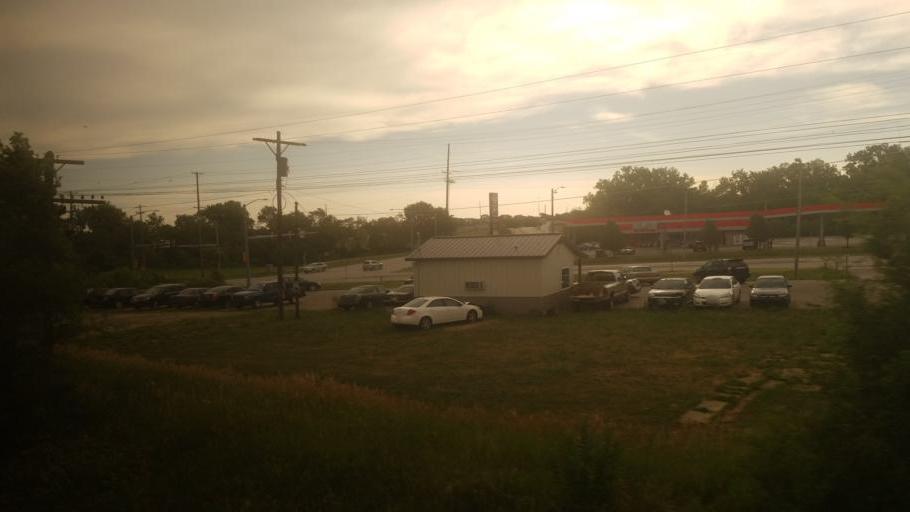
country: US
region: Kansas
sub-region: Shawnee County
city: Topeka
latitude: 38.9847
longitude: -95.6886
